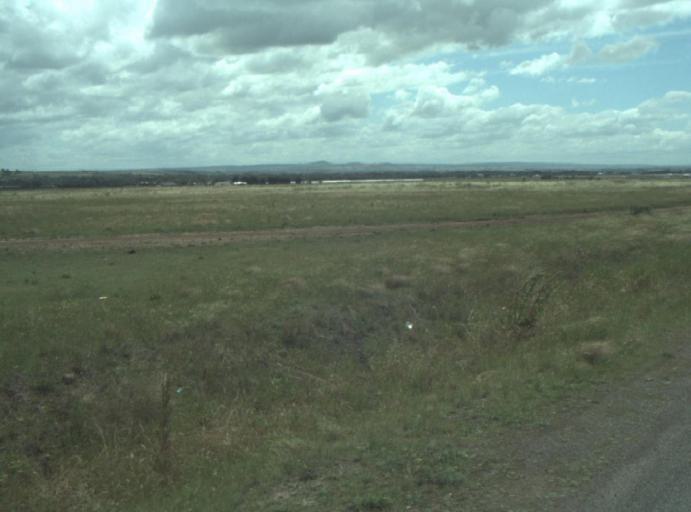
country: AU
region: Victoria
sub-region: Greater Geelong
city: Lara
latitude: -38.0487
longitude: 144.3803
